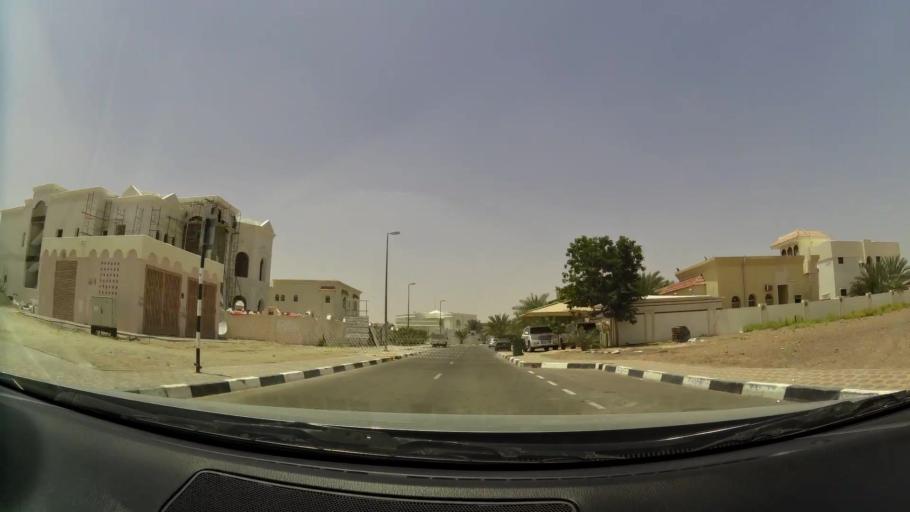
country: OM
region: Al Buraimi
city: Al Buraymi
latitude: 24.2629
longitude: 55.7118
